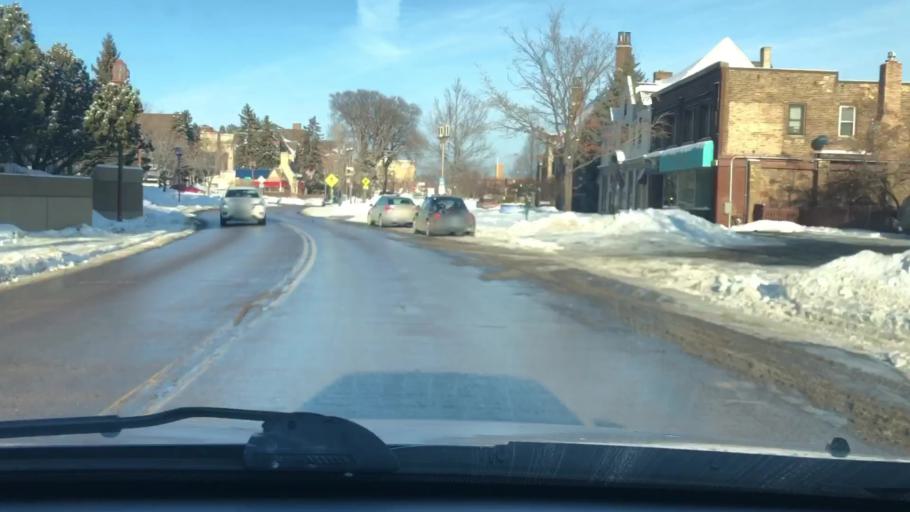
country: US
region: Minnesota
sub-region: Saint Louis County
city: Duluth
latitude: 46.7938
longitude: -92.0892
